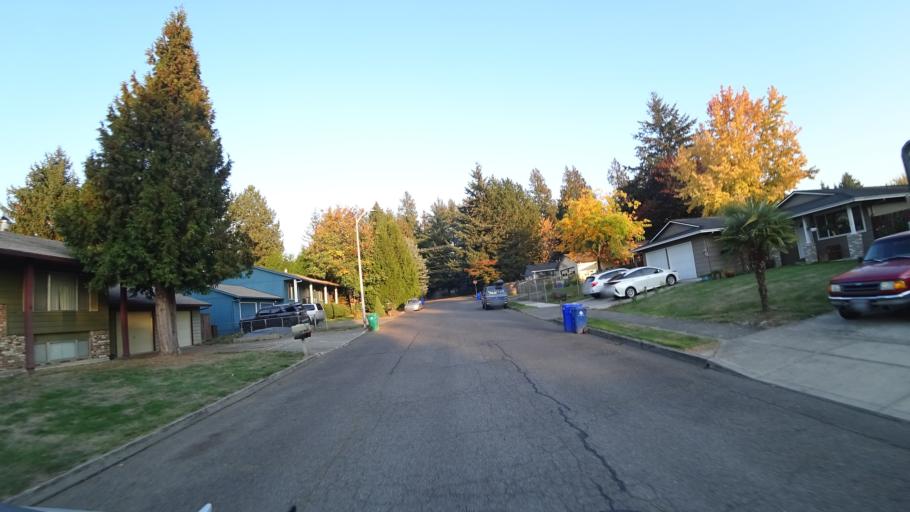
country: US
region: Oregon
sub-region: Multnomah County
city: Gresham
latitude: 45.5169
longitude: -122.4458
